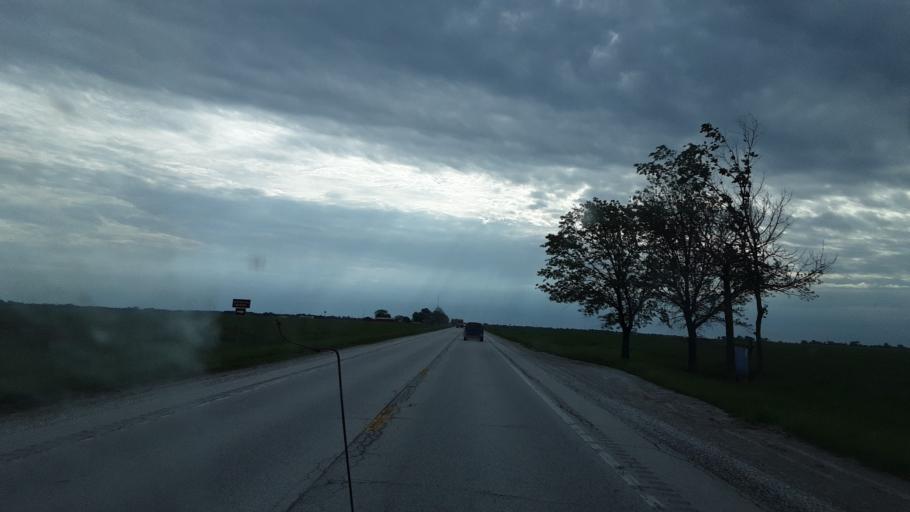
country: US
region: Illinois
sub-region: Hancock County
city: Carthage
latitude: 40.4030
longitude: -91.1928
